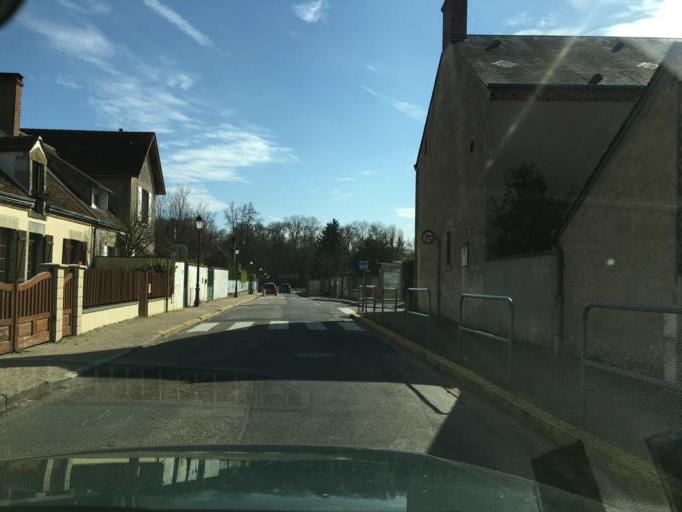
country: FR
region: Centre
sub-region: Departement du Loiret
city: Vitry-aux-Loges
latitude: 47.9397
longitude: 2.2681
